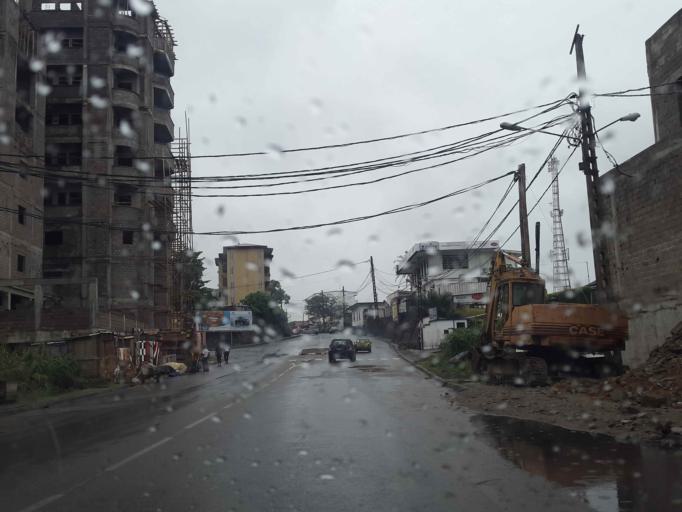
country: CM
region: Littoral
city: Douala
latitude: 4.0422
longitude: 9.6916
